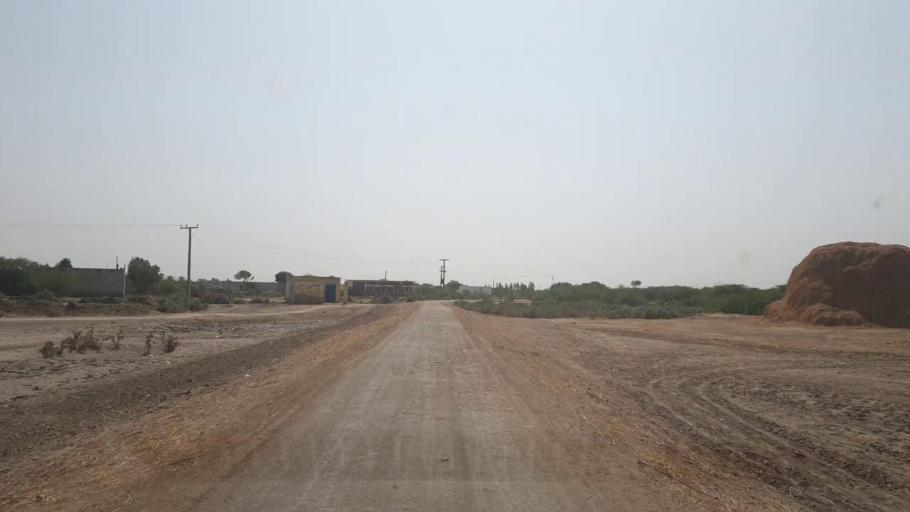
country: PK
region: Sindh
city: Jati
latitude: 24.4696
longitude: 68.5568
